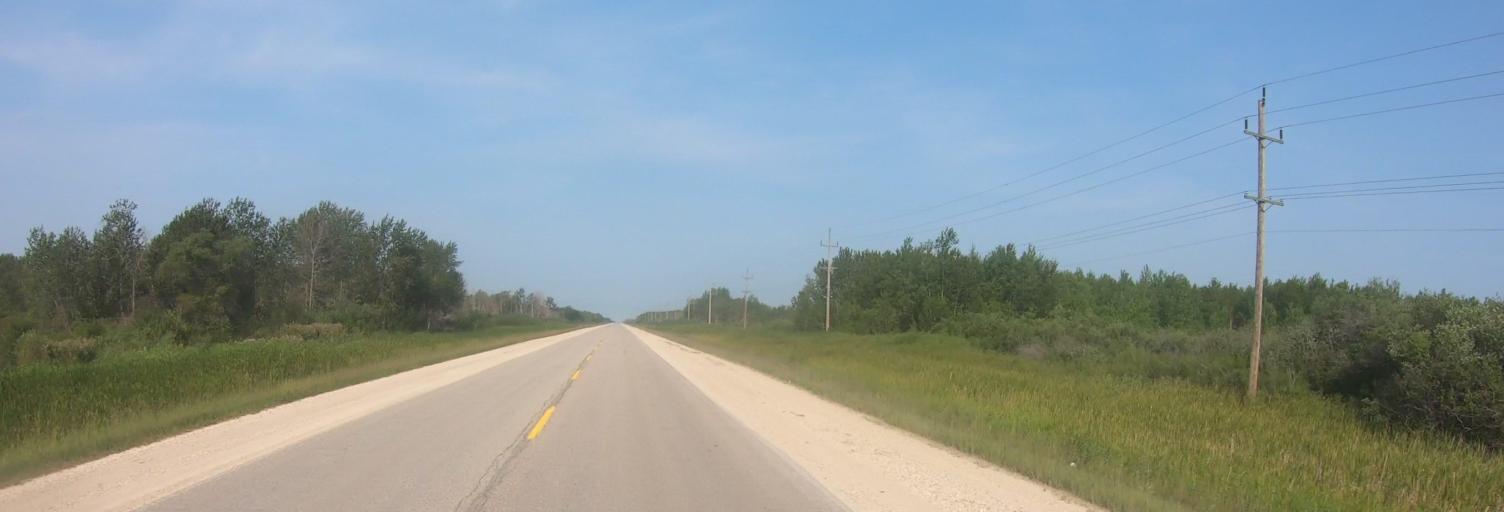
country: CA
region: Manitoba
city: La Broquerie
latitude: 49.2888
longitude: -96.5206
